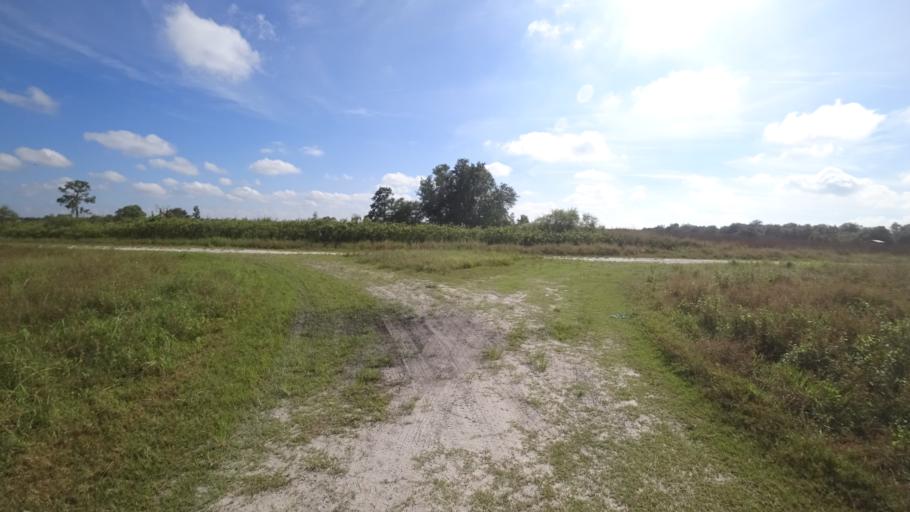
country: US
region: Florida
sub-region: Sarasota County
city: Lake Sarasota
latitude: 27.3726
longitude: -82.1602
